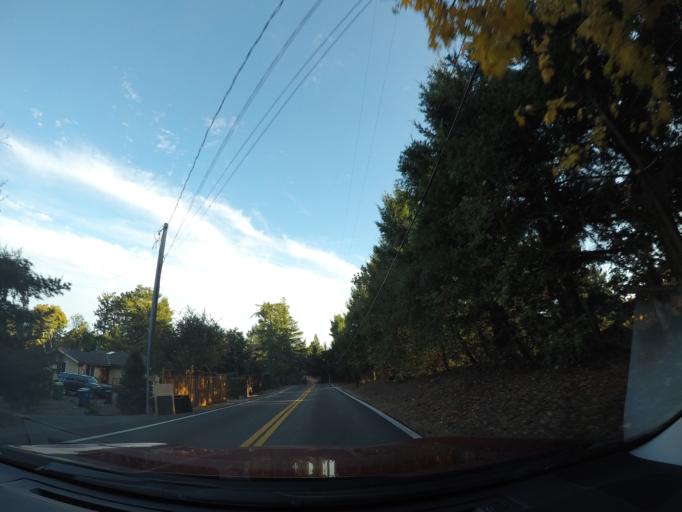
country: US
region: California
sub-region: Santa Clara County
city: Lexington Hills
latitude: 37.1509
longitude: -121.9957
